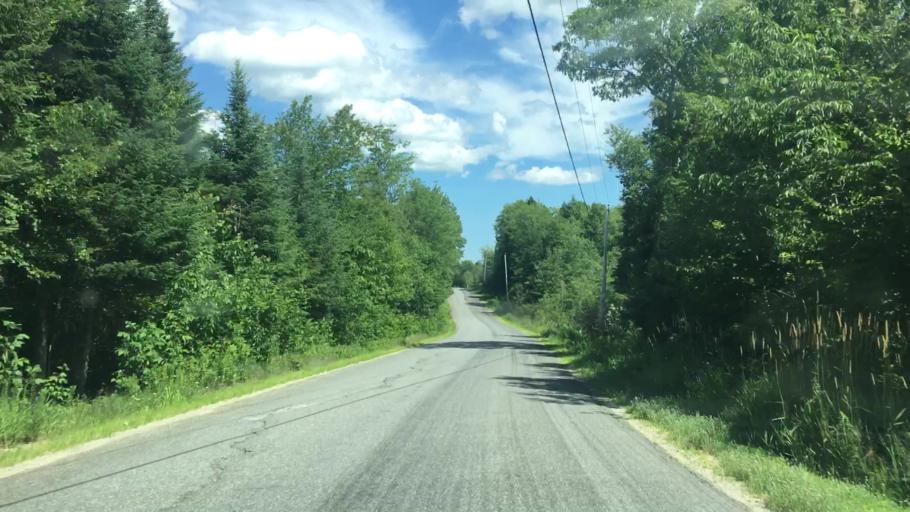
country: US
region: Maine
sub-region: Franklin County
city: Chesterville
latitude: 44.5548
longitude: -70.1079
